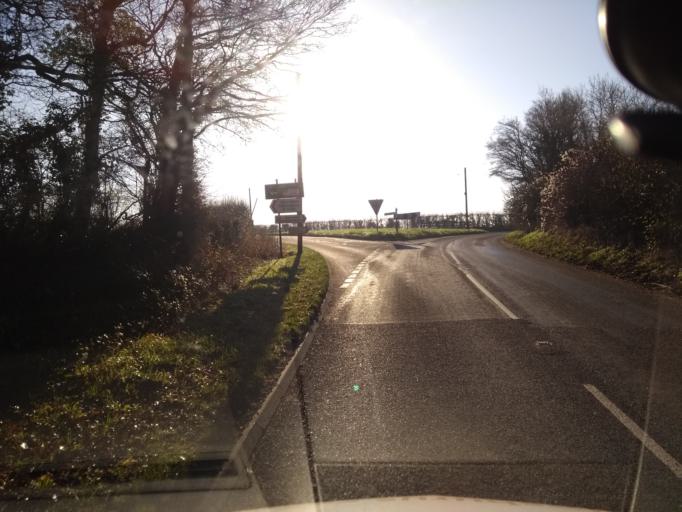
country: GB
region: England
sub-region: Somerset
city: Redlynch
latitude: 51.0868
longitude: -2.4133
